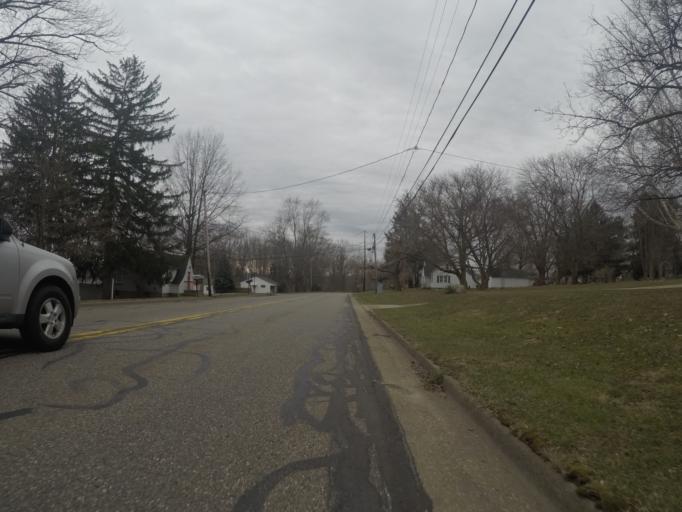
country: US
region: Ohio
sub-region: Portage County
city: Ravenna
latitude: 41.1617
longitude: -81.2723
